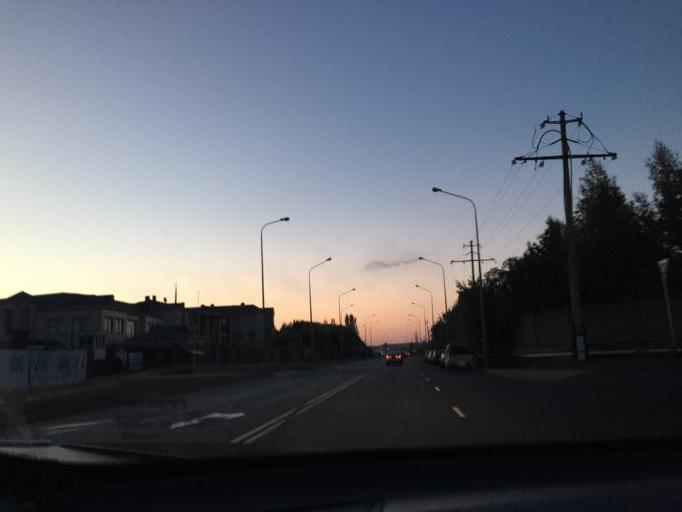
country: KZ
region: Astana Qalasy
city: Astana
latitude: 51.1434
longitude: 71.4536
